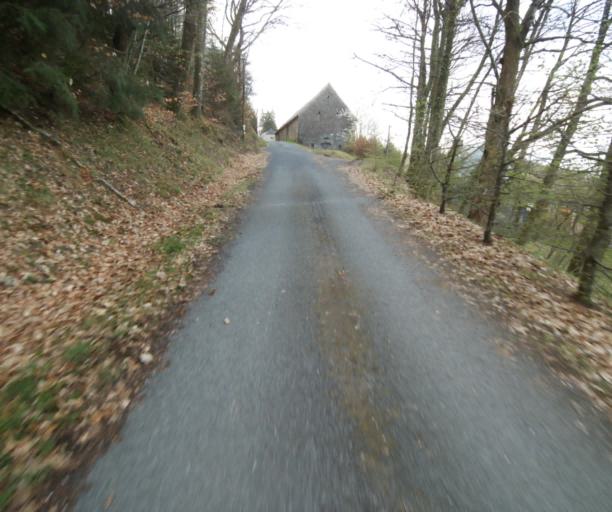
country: FR
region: Limousin
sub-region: Departement de la Correze
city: Correze
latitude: 45.3655
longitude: 1.8515
